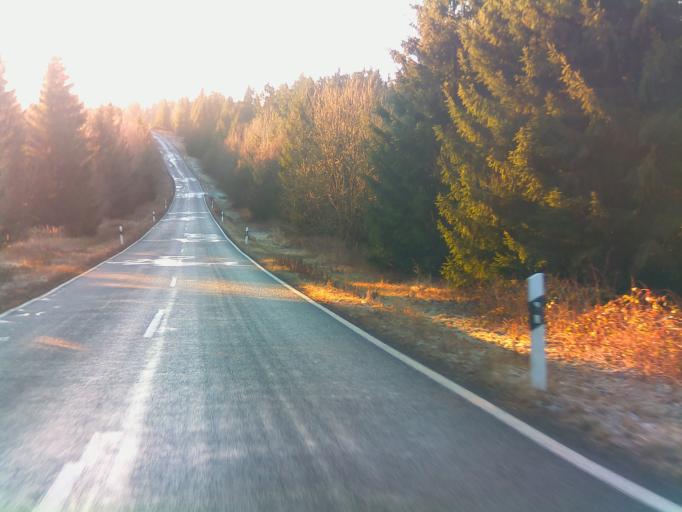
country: DE
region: Bavaria
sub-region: Upper Franconia
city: Tettau
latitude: 50.4633
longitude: 11.2504
